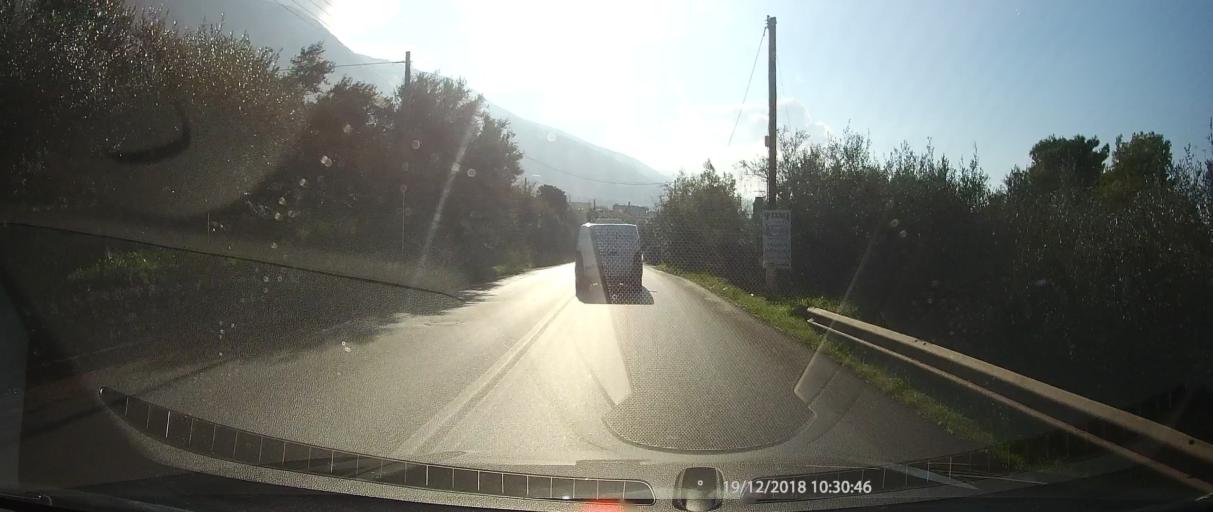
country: GR
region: Peloponnese
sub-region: Nomos Messinias
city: Paralia Vergas
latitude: 37.0135
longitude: 22.1538
